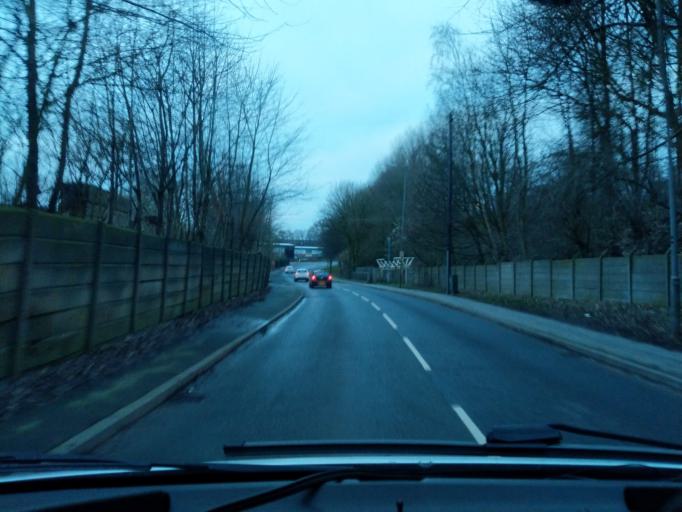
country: GB
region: England
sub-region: St. Helens
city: St Helens
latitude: 53.4617
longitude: -2.7308
